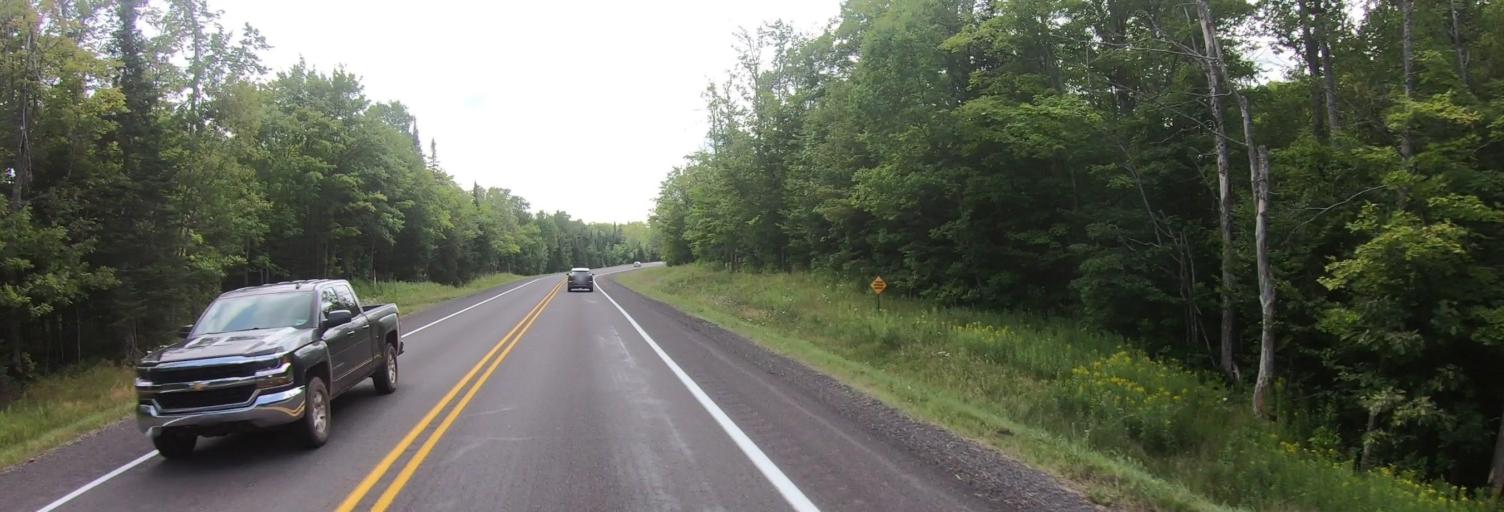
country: US
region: Michigan
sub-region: Houghton County
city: Hancock
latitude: 47.0220
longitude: -88.7355
